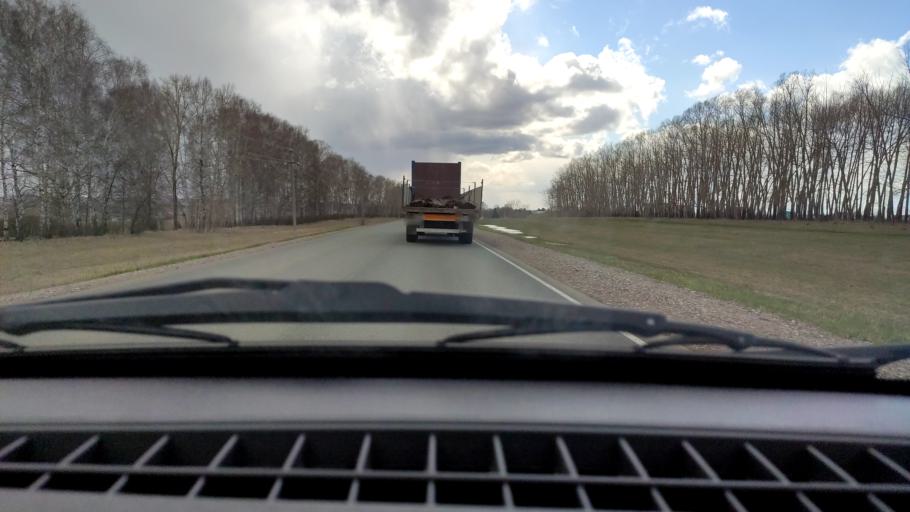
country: RU
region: Bashkortostan
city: Kushnarenkovo
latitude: 55.0550
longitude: 55.1492
